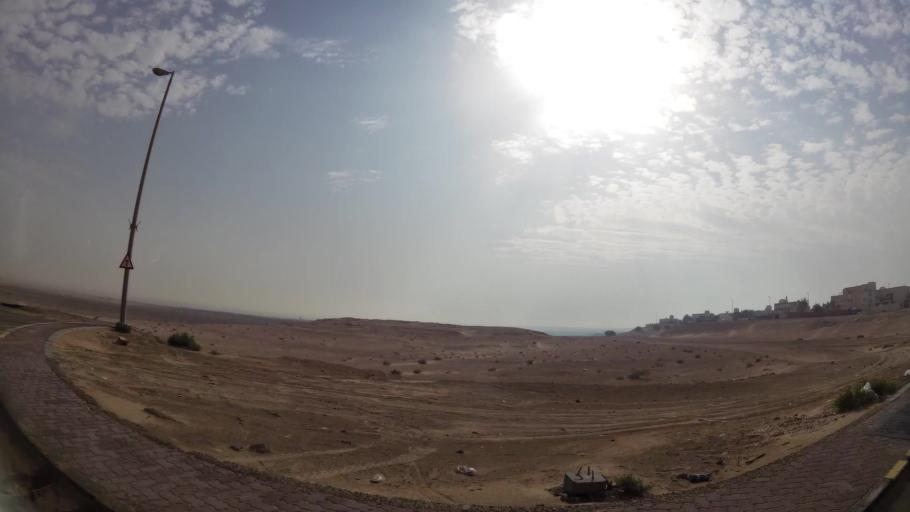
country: AE
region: Abu Dhabi
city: Abu Dhabi
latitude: 24.2567
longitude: 54.7221
